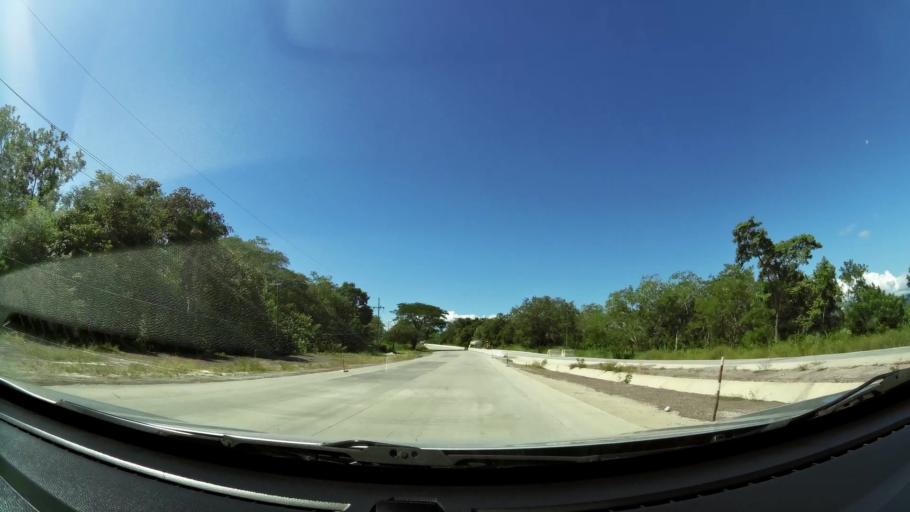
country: CR
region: Guanacaste
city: Liberia
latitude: 10.5600
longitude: -85.3797
